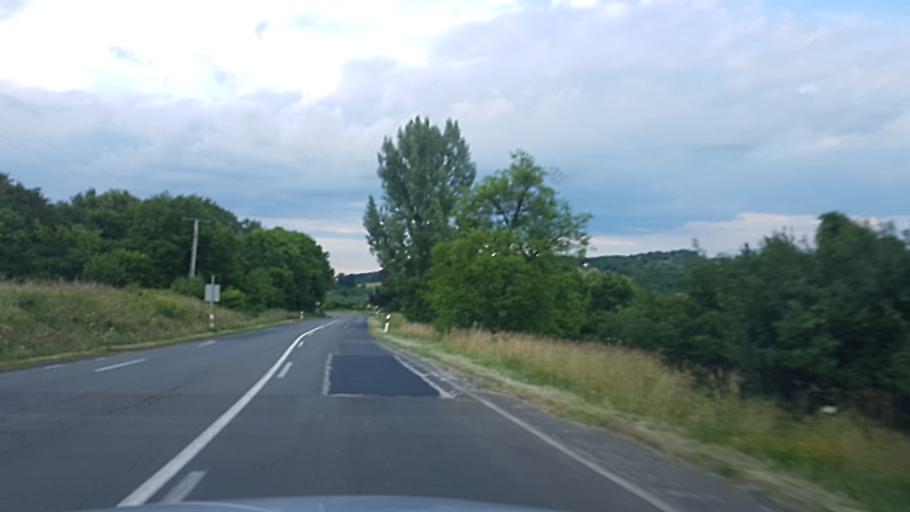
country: HU
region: Somogy
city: Kaposvar
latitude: 46.2794
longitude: 17.8212
